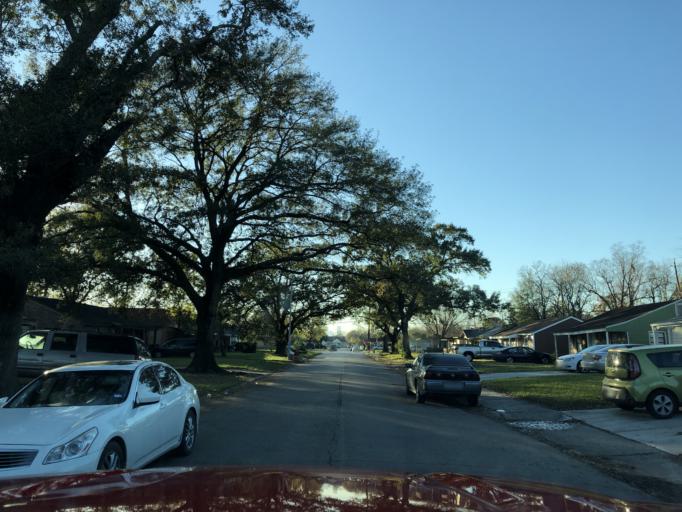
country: US
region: Texas
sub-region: Harris County
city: Jacinto City
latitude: 29.7626
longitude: -95.2686
